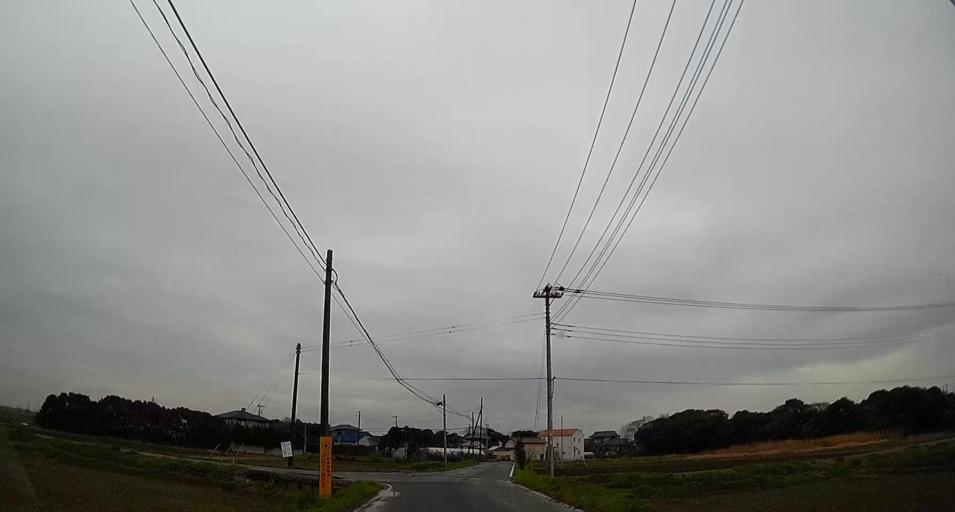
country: JP
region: Chiba
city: Kisarazu
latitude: 35.4224
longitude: 139.9092
